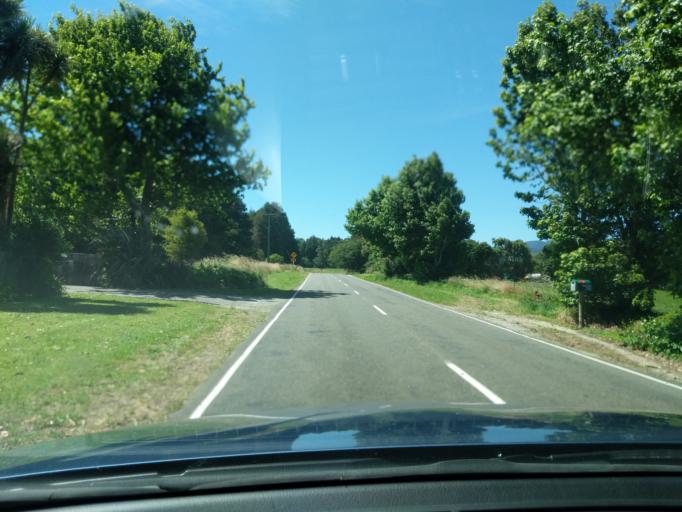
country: NZ
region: Tasman
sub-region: Tasman District
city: Takaka
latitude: -40.7028
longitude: 172.6341
